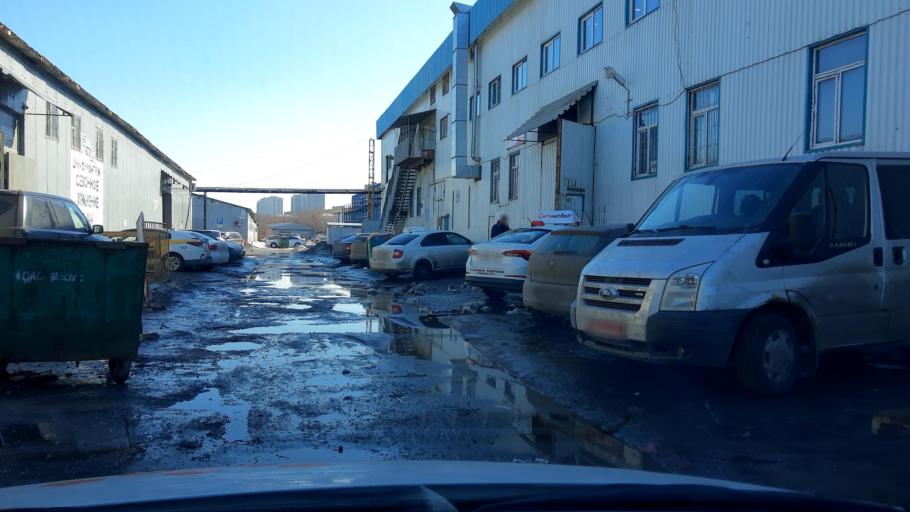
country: RU
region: Moscow
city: Novyye Cheremushki
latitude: 55.7009
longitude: 37.5903
